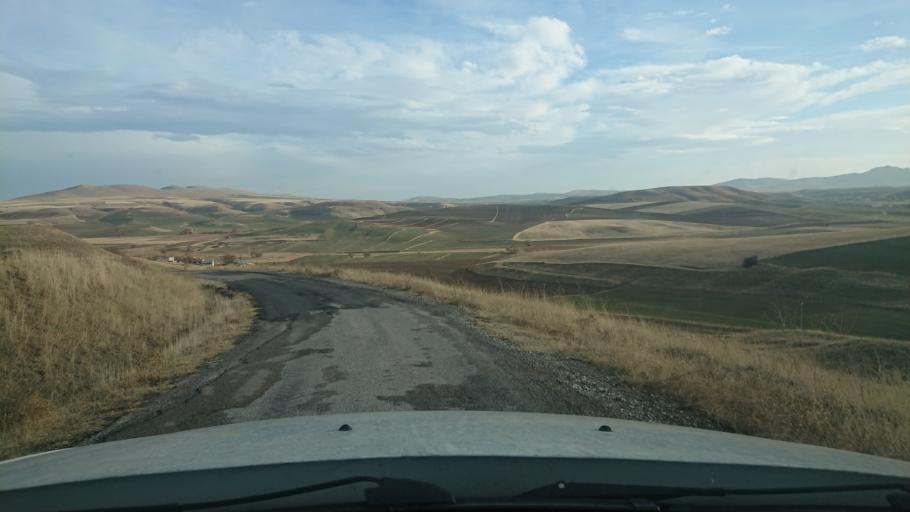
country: TR
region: Aksaray
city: Acipinar
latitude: 38.6712
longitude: 33.8629
